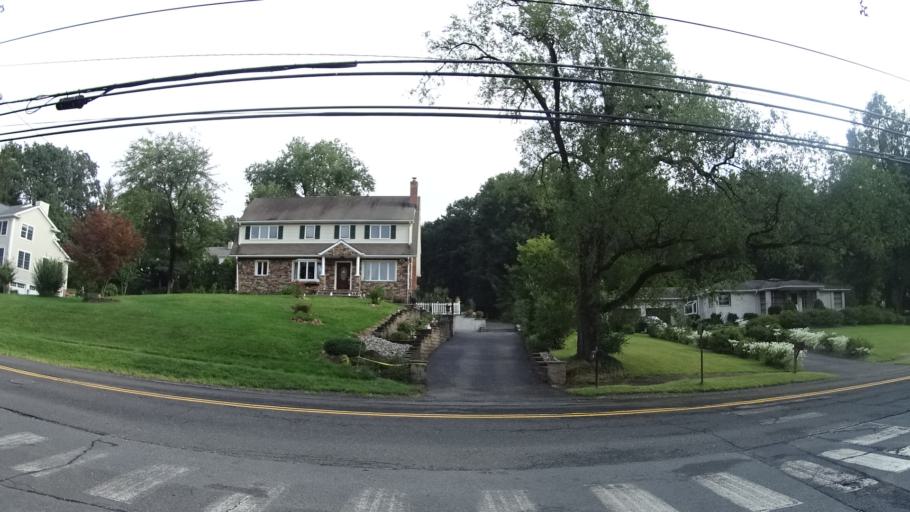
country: US
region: New Jersey
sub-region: Union County
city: Berkeley Heights
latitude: 40.7045
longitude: -74.4345
